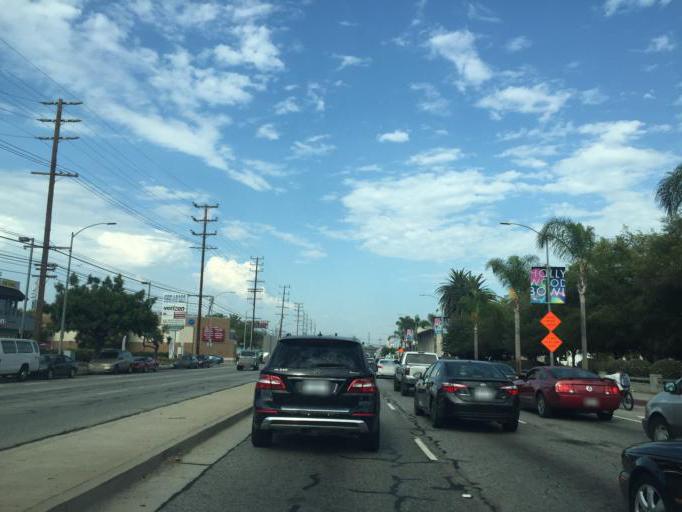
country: US
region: California
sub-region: Los Angeles County
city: Culver City
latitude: 34.0260
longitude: -118.3942
